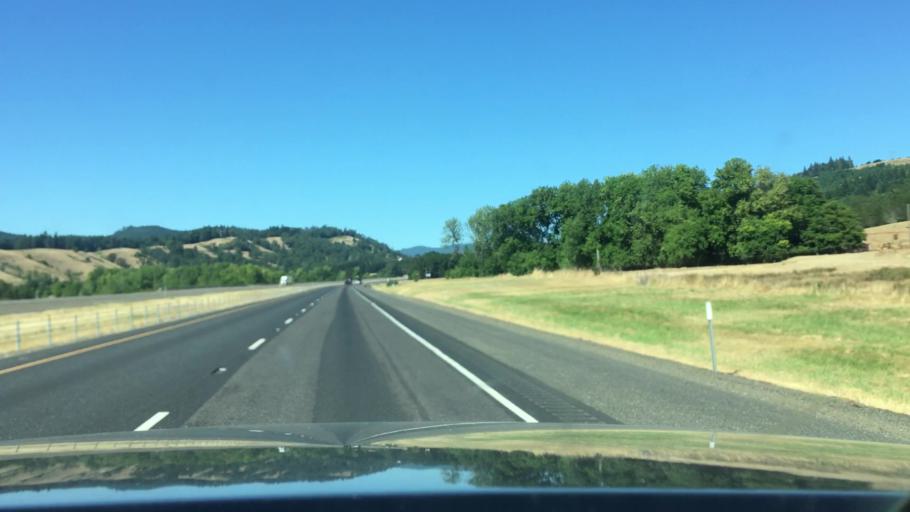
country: US
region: Oregon
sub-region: Douglas County
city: Yoncalla
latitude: 43.5872
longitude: -123.2528
